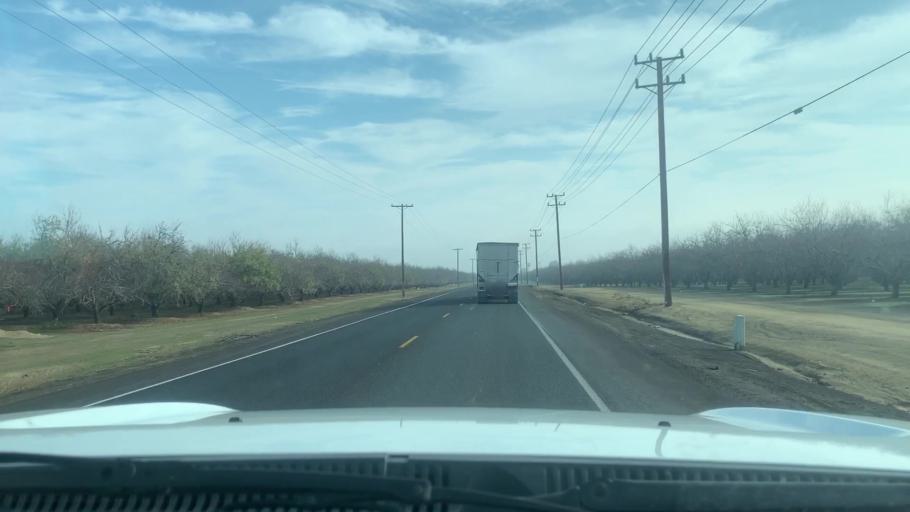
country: US
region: California
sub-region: Kern County
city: Lost Hills
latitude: 35.4992
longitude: -119.6827
